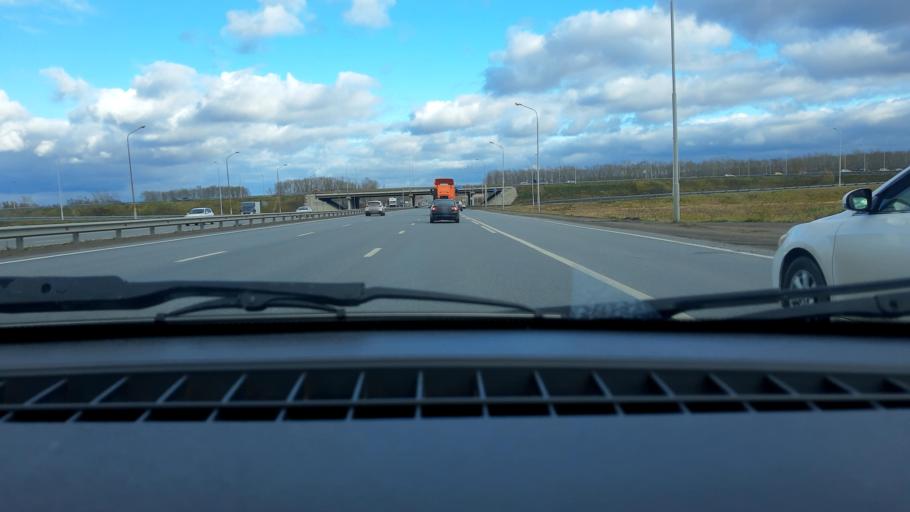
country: RU
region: Bashkortostan
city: Kabakovo
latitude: 54.6505
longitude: 56.0780
